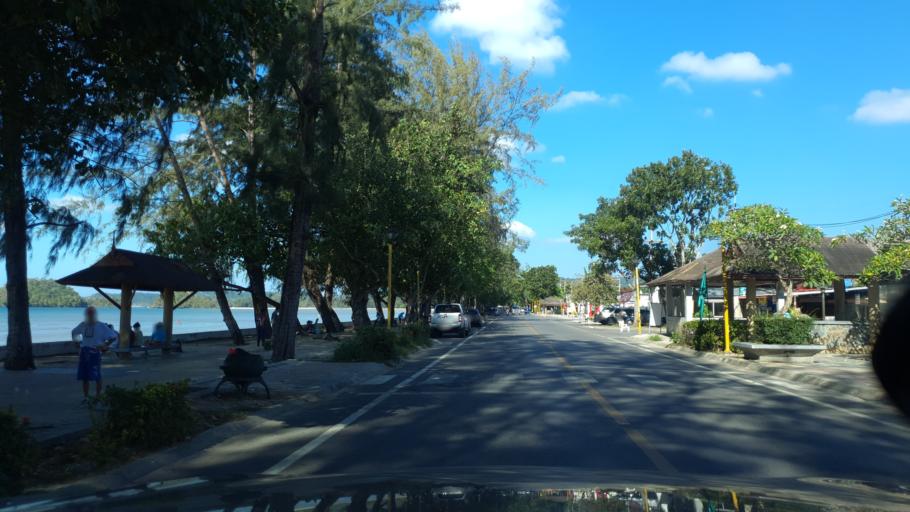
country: TH
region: Phangnga
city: Ban Ao Nang
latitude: 8.0420
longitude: 98.8117
